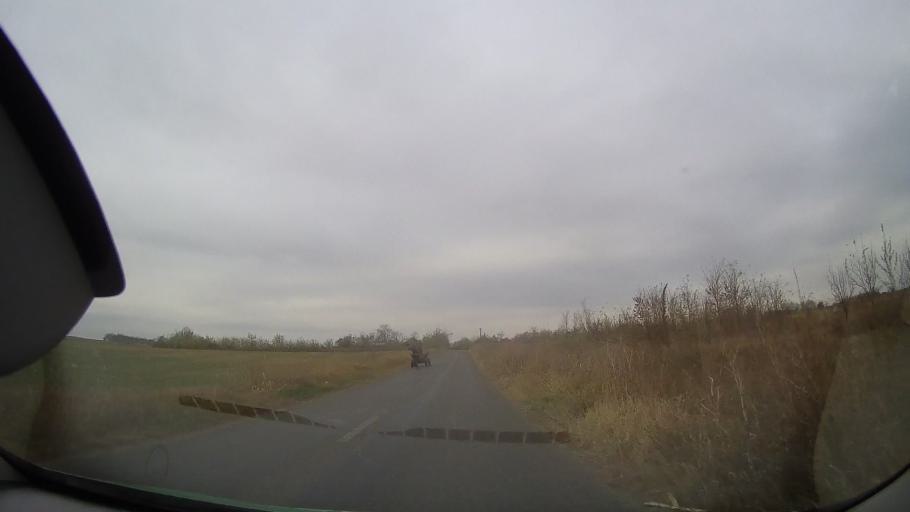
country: RO
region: Buzau
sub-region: Comuna Largu
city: Largu
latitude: 44.9696
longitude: 27.1839
